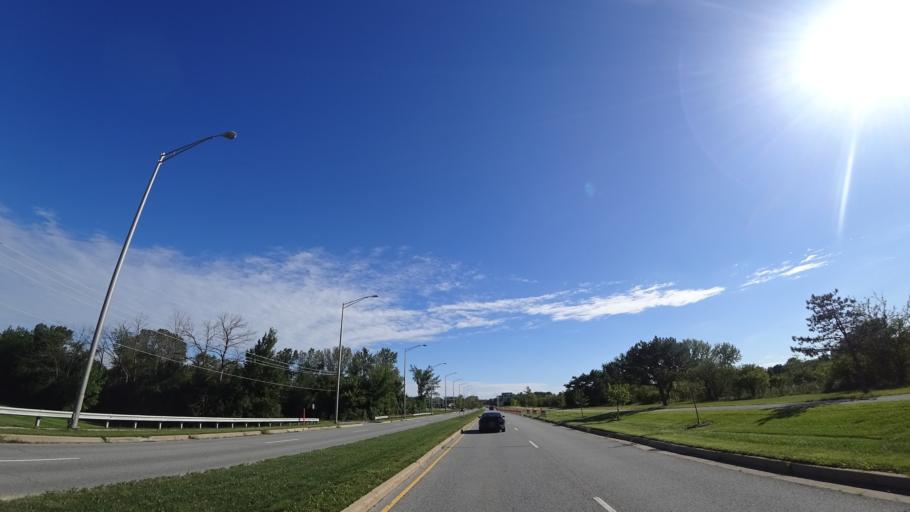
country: US
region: Illinois
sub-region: Cook County
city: Oak Forest
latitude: 41.5928
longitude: -87.7361
